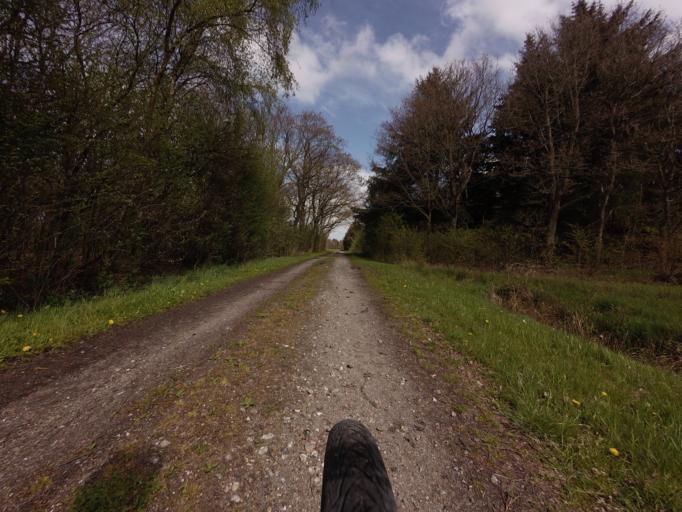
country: DK
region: North Denmark
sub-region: Jammerbugt Kommune
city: Kas
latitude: 57.1937
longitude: 9.5935
